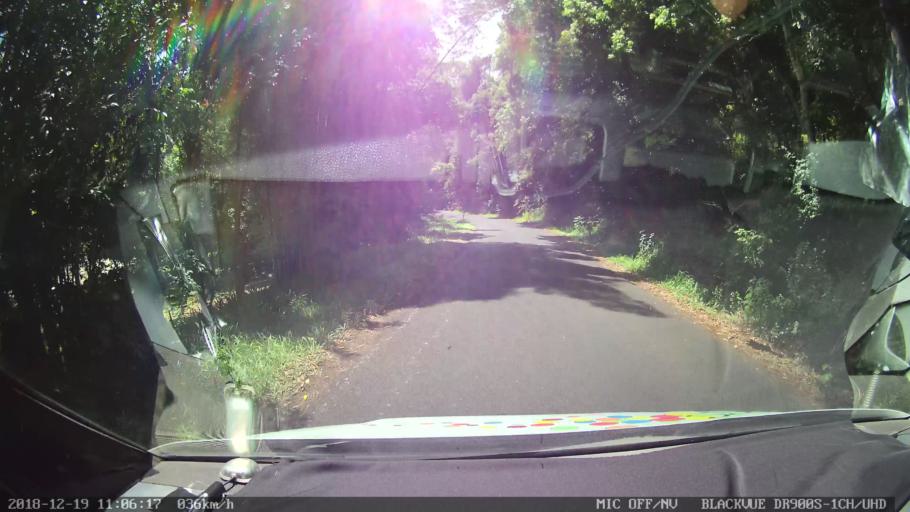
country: AU
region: New South Wales
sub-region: Lismore Municipality
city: Nimbin
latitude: -28.6217
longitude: 153.2657
